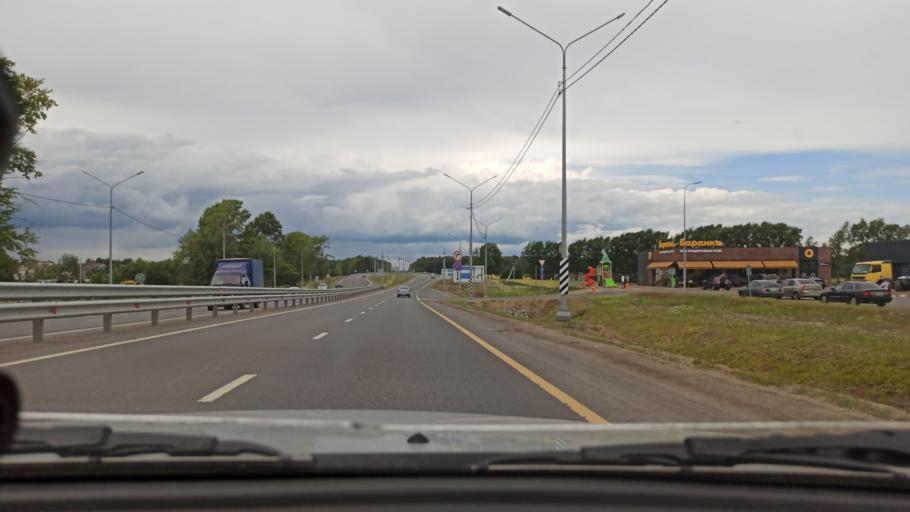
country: RU
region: Vologda
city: Molochnoye
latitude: 59.2615
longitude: 39.7469
